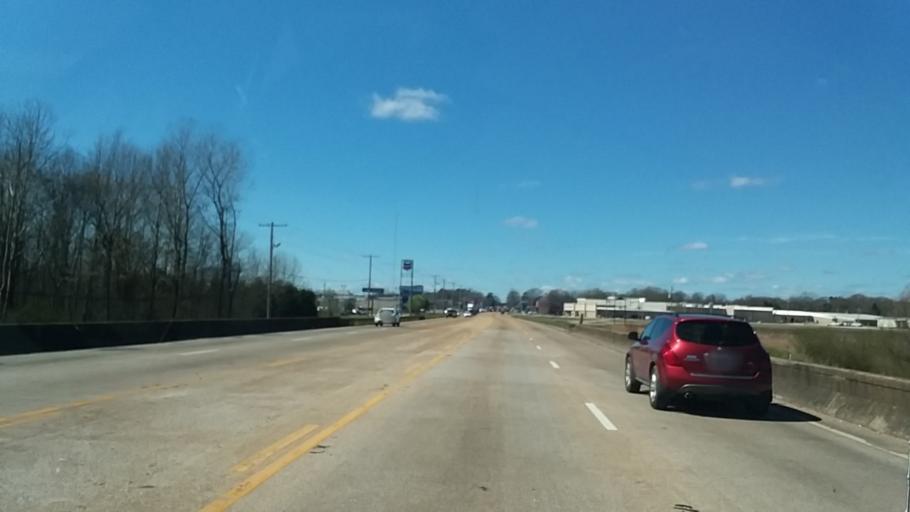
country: US
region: Mississippi
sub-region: Alcorn County
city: Corinth
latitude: 34.9110
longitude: -88.4954
